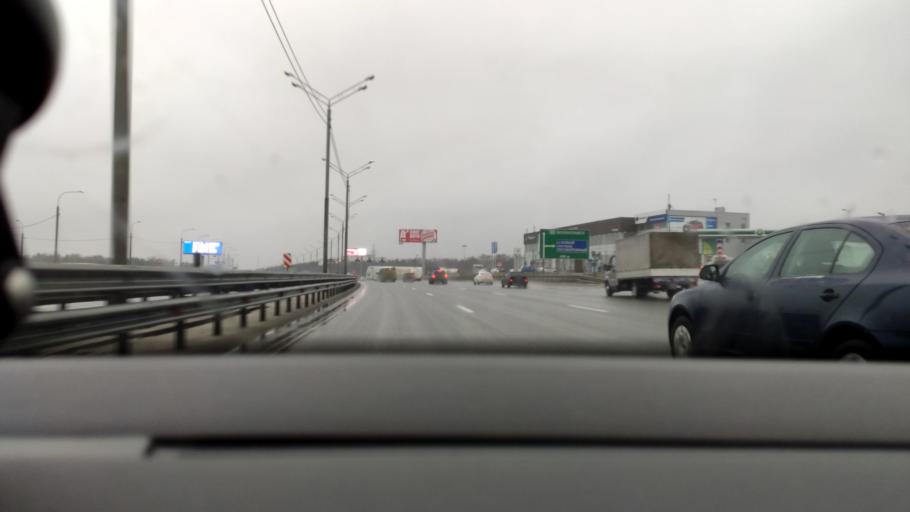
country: RU
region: Moskovskaya
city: Arkhangel'skoye
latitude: 55.8029
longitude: 37.3017
